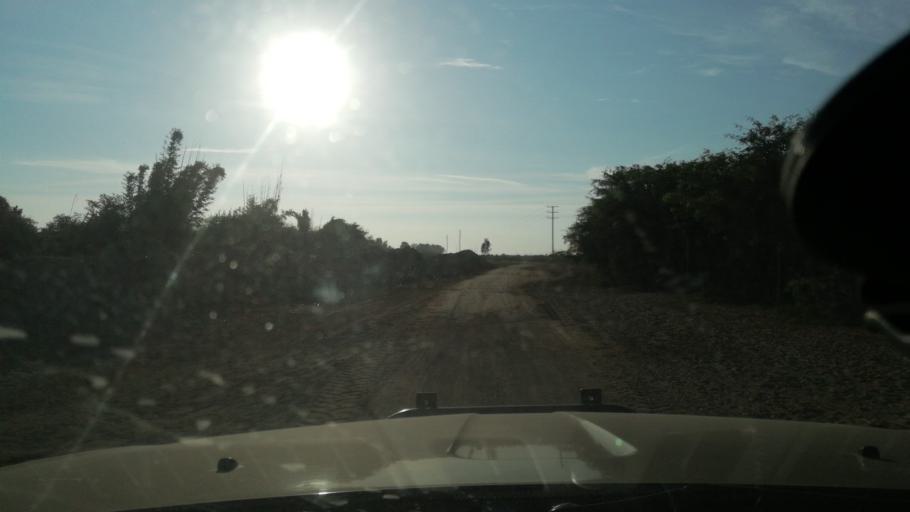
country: PE
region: Ica
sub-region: Provincia de Chincha
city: San Pedro
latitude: -13.3380
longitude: -76.1656
